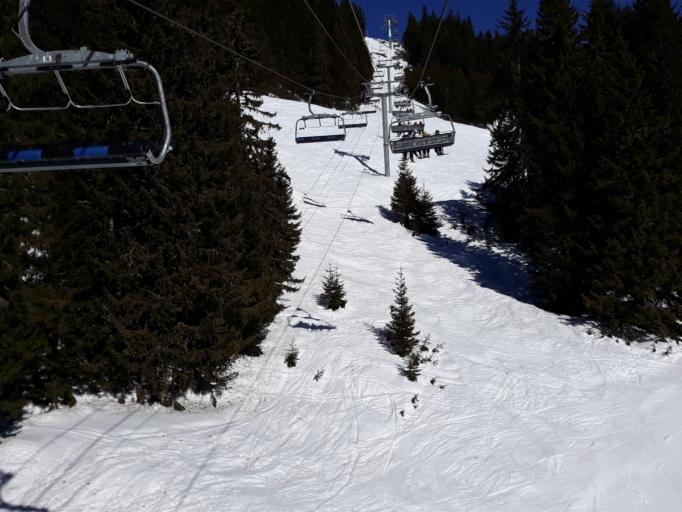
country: FR
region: Rhone-Alpes
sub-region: Departement de la Haute-Savoie
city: Araches-la-Frasse
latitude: 46.0304
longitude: 6.6751
